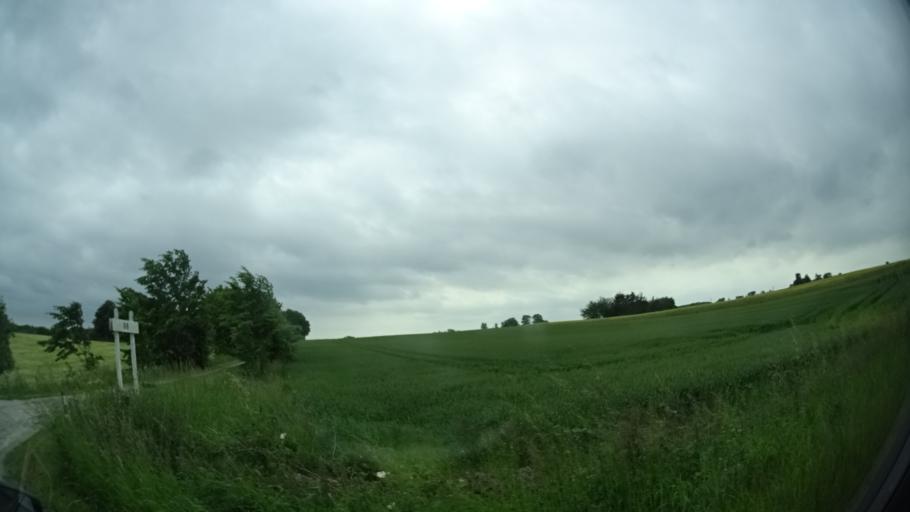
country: DK
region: Central Jutland
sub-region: Arhus Kommune
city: Marslet
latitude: 56.0425
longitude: 10.1665
